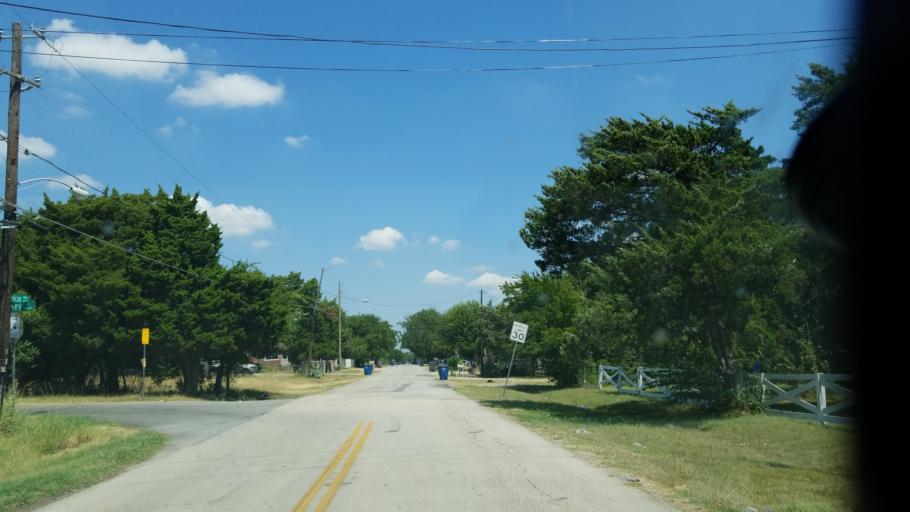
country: US
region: Texas
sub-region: Dallas County
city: Duncanville
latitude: 32.6647
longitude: -96.8841
